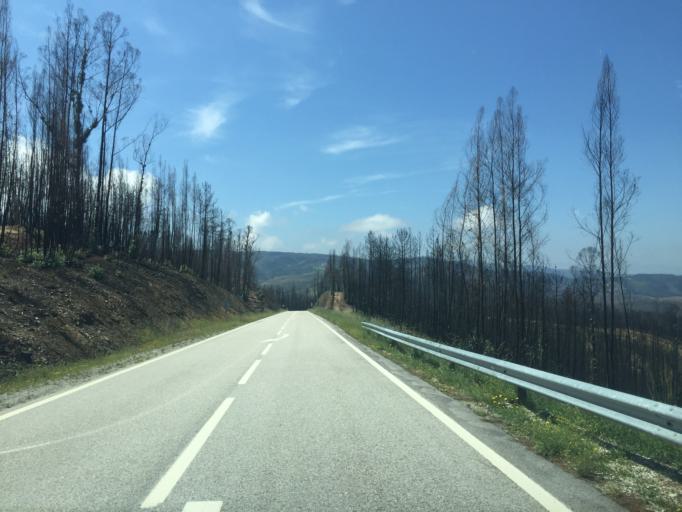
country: PT
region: Coimbra
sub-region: Pampilhosa da Serra
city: Pampilhosa da Serra
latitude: 39.9966
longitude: -7.9727
